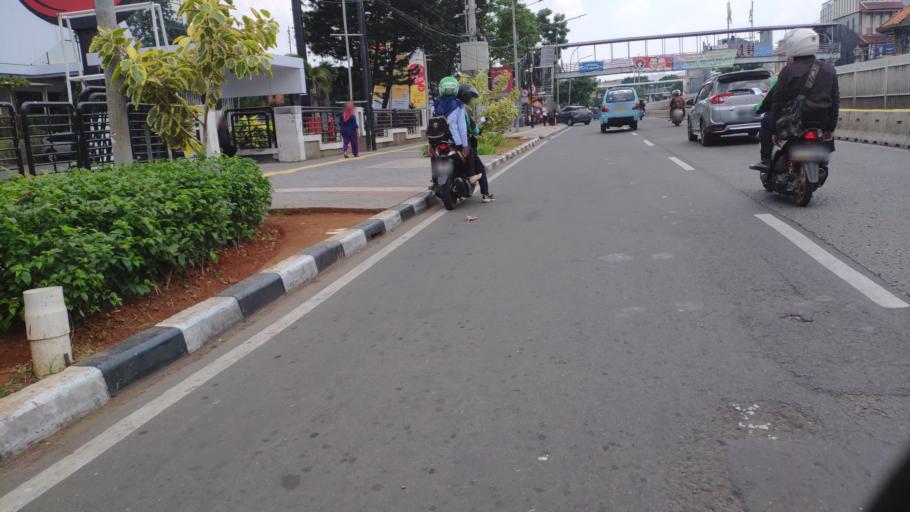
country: ID
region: Jakarta Raya
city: Jakarta
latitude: -6.2145
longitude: 106.8643
